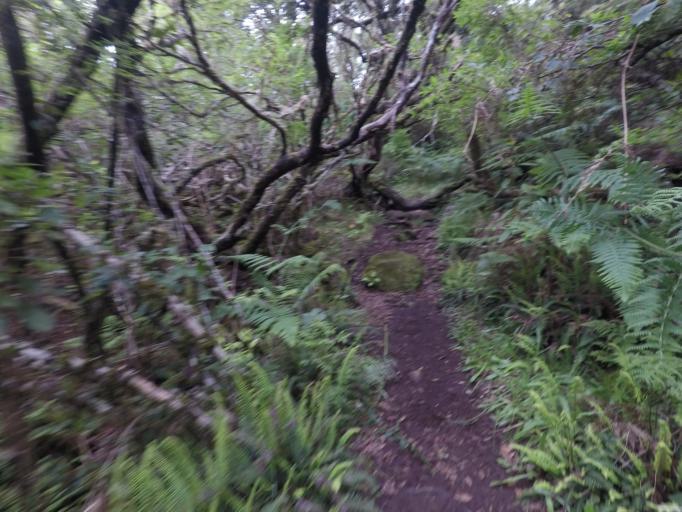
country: PT
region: Madeira
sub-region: Sao Vicente
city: Sao Vicente
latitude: 32.7690
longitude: -17.0602
